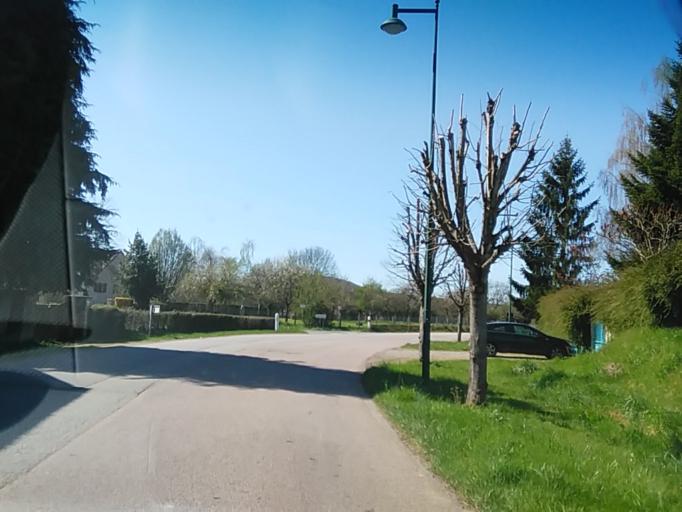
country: FR
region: Lower Normandy
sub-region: Departement de l'Orne
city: Conde-sur-Sarthe
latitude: 48.4662
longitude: 0.0204
